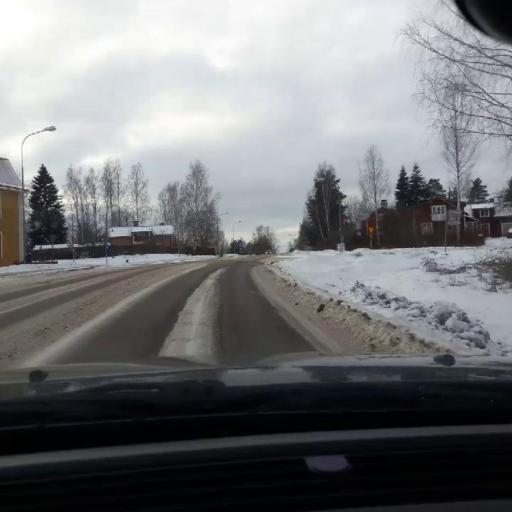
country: SE
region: Gaevleborg
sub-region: Bollnas Kommun
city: Bollnas
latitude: 61.3340
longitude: 16.3920
